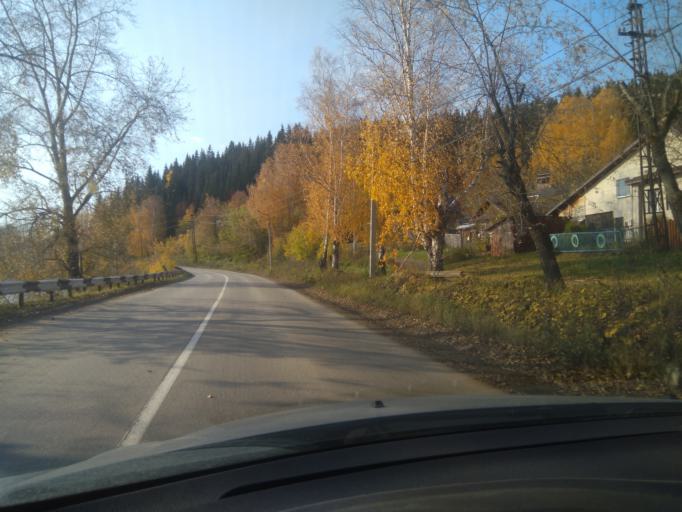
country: RU
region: Sverdlovsk
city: Nizhniye Sergi
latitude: 56.6743
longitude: 59.3203
